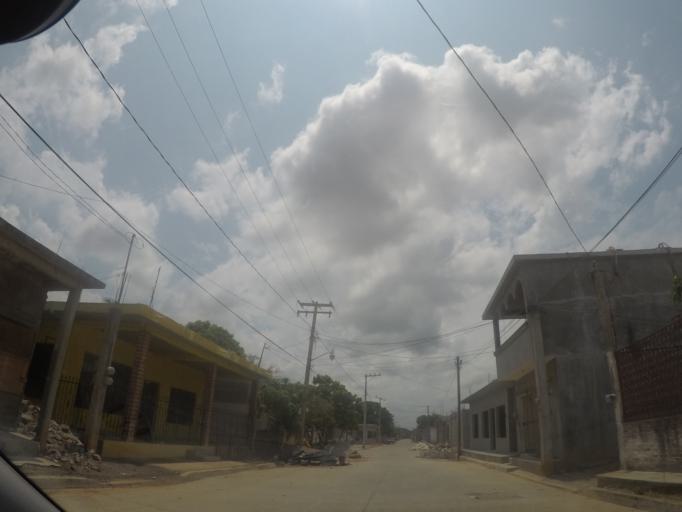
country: MX
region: Oaxaca
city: El Espinal
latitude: 16.5543
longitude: -94.9470
